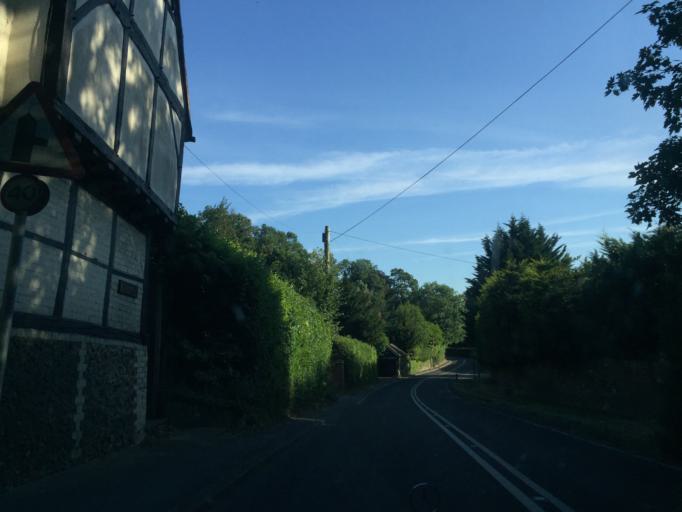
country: GB
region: England
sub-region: Wokingham
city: Wargrave
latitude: 51.5082
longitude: -0.8683
